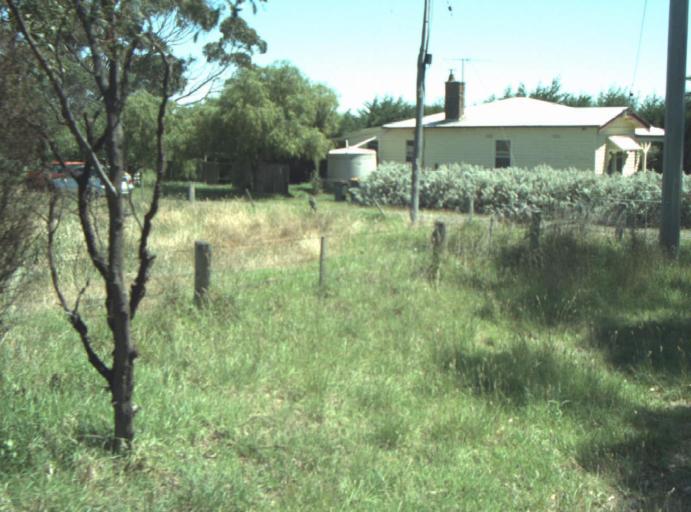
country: AU
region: Victoria
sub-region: Greater Geelong
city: Breakwater
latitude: -38.2157
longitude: 144.3575
